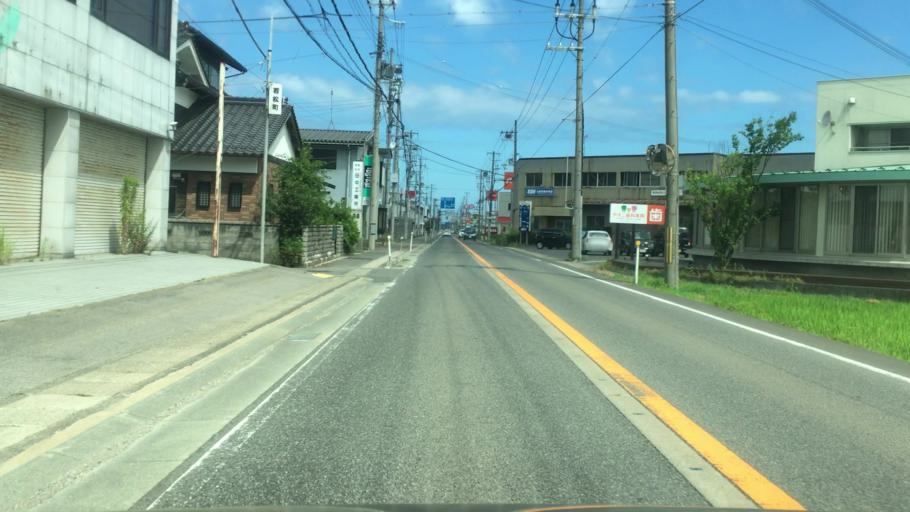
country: JP
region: Tottori
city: Tottori
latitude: 35.6126
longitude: 134.4682
